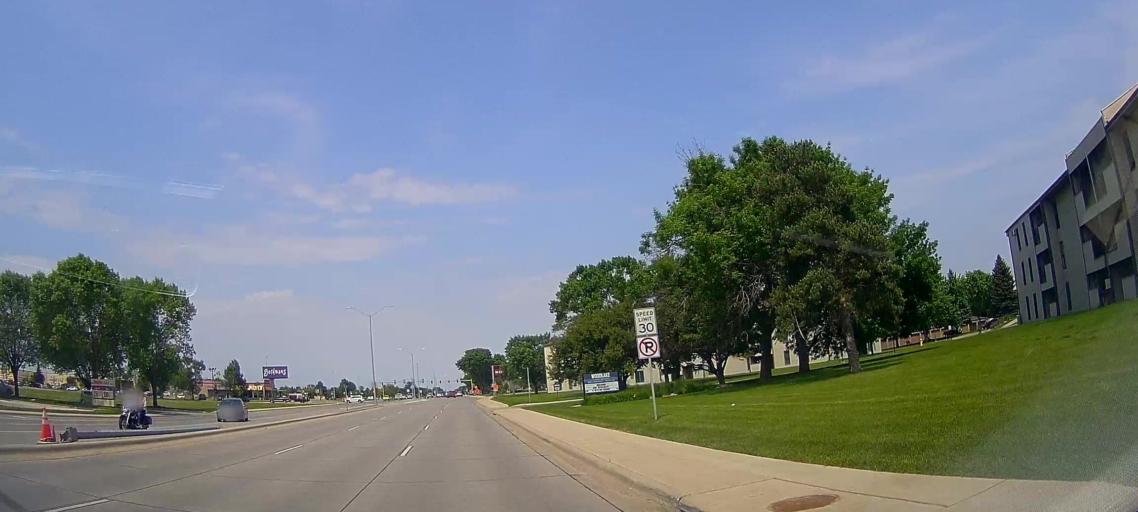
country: US
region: South Dakota
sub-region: Minnehaha County
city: Sioux Falls
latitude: 43.5081
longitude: -96.7710
